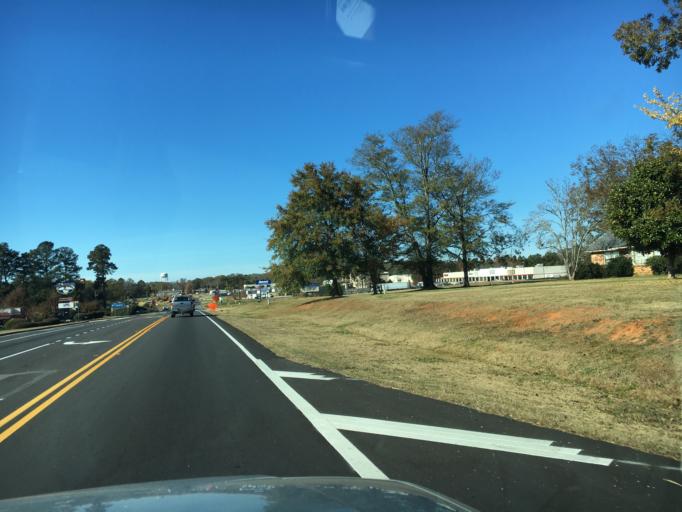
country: US
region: Georgia
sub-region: Hart County
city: Hartwell
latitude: 34.3514
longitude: -82.9030
